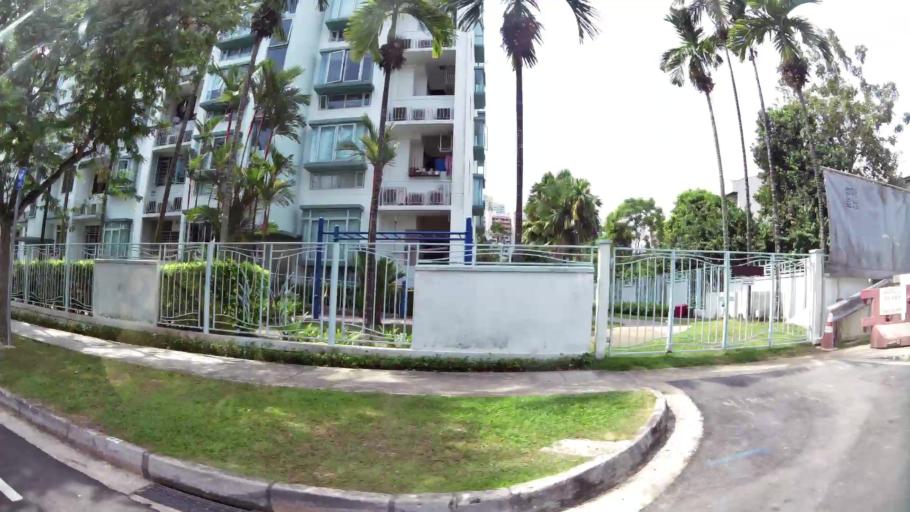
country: SG
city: Singapore
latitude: 1.3244
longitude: 103.7660
